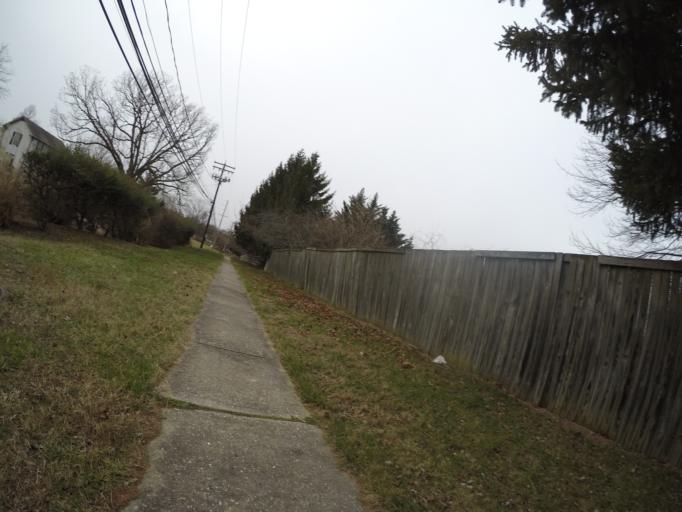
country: US
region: Maryland
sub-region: Howard County
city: Ilchester
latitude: 39.2144
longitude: -76.7826
